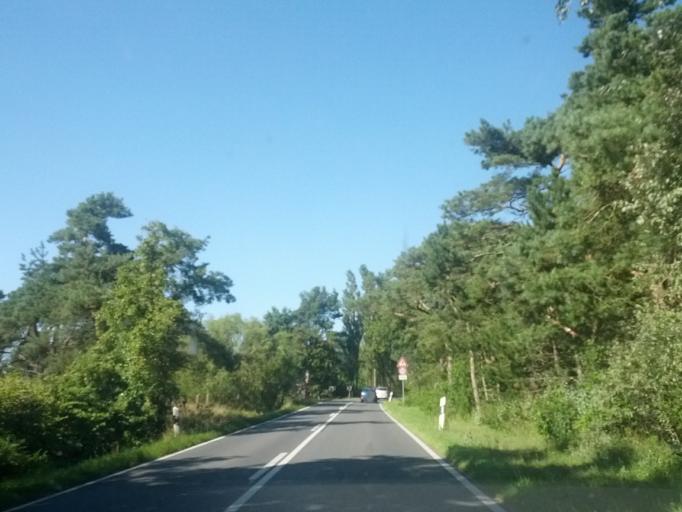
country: DE
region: Mecklenburg-Vorpommern
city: Ostseebad Gohren
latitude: 54.3101
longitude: 13.7158
